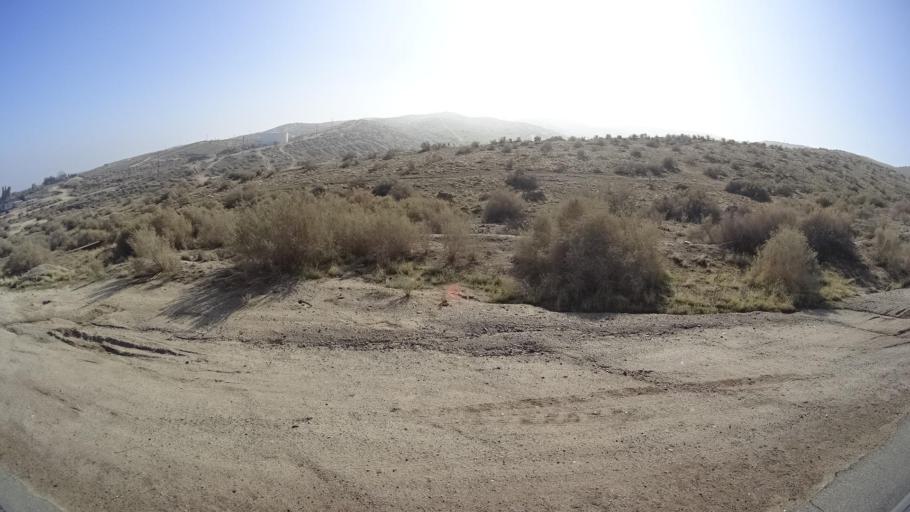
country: US
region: California
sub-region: Kern County
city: Taft Heights
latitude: 35.1307
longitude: -119.4687
